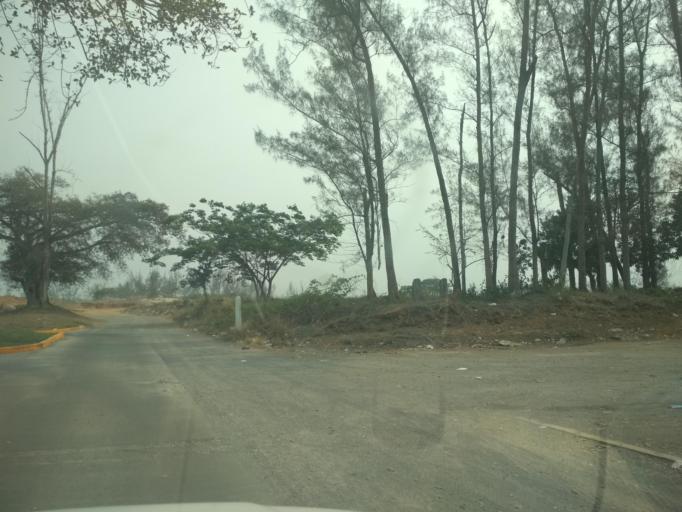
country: MX
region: Veracruz
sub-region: Veracruz
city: Las Amapolas
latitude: 19.1473
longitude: -96.2239
